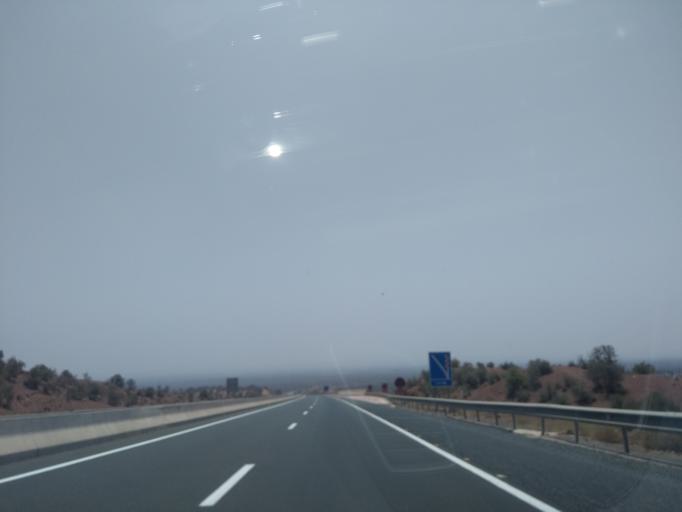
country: MA
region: Souss-Massa-Draa
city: Oulad Teima
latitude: 30.5422
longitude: -9.3253
